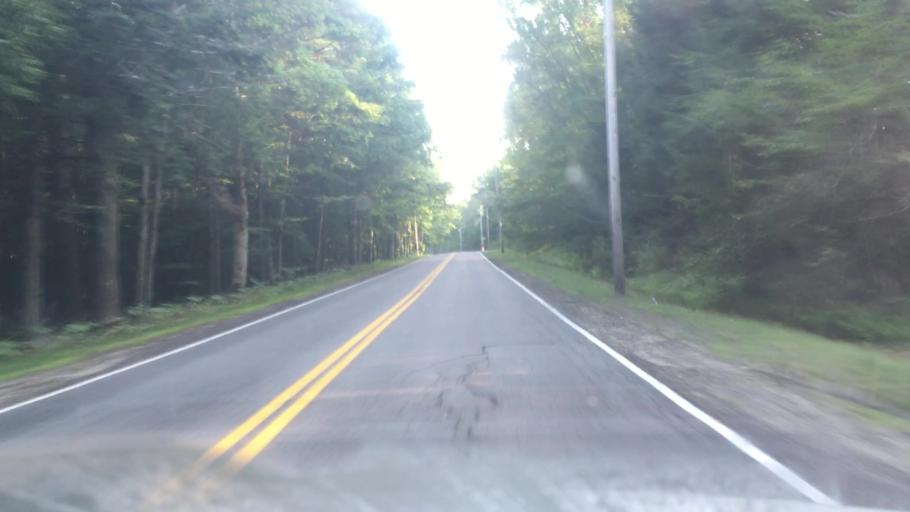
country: US
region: Maine
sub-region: Cumberland County
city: Freeport
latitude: 43.9280
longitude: -70.0875
